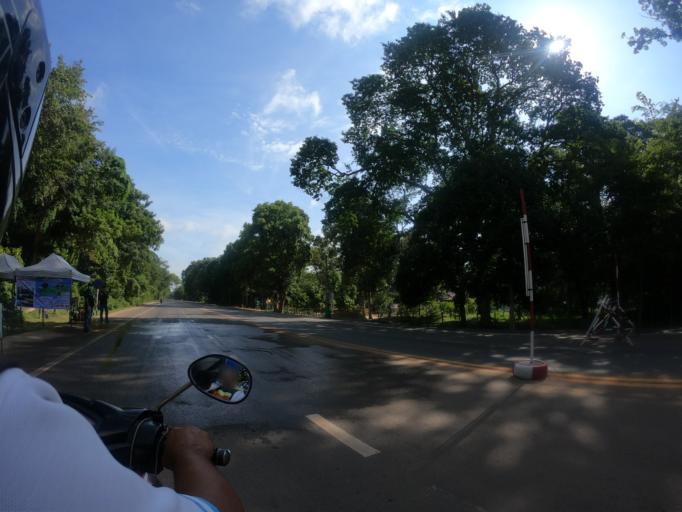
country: TH
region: Surin
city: Kap Choeng
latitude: 14.4414
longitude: 103.7007
